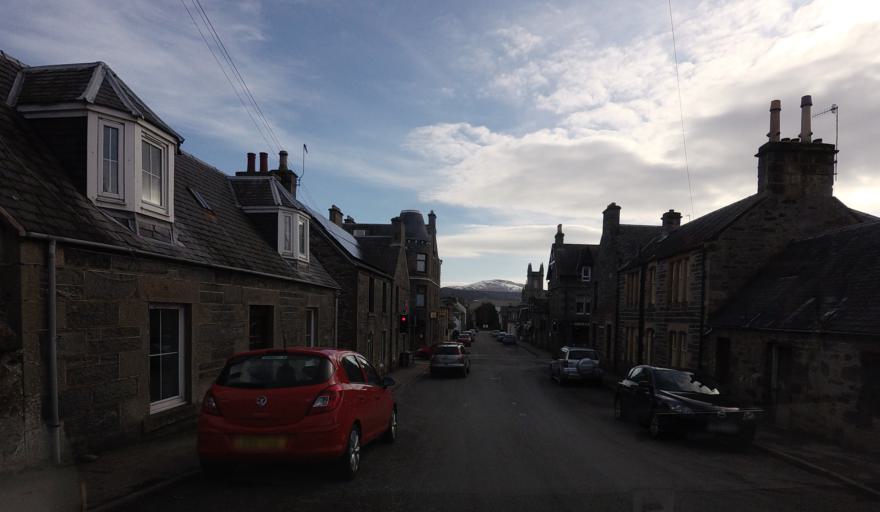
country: GB
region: Scotland
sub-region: Highland
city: Kingussie
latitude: 57.0806
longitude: -4.0514
